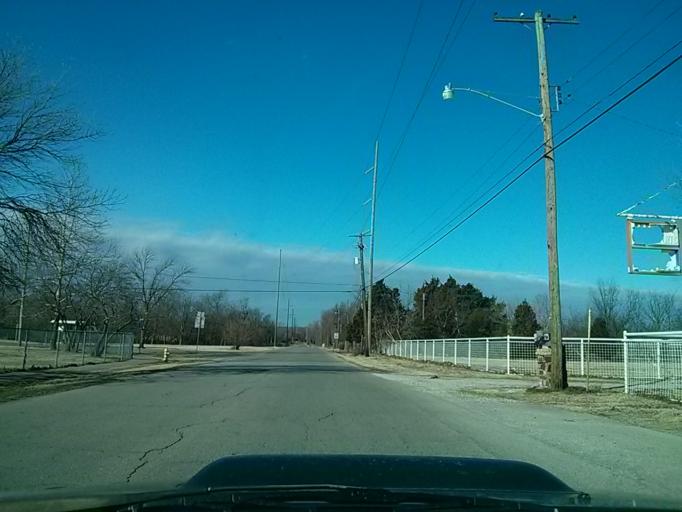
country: US
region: Oklahoma
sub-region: Tulsa County
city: Turley
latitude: 36.2134
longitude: -95.9508
